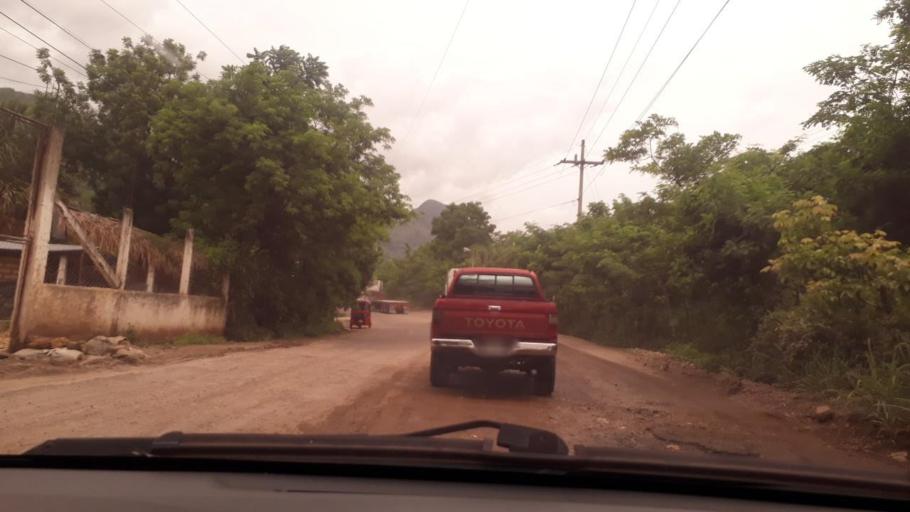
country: GT
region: Chiquimula
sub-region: Municipio de Jocotan
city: Jocotan
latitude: 14.7960
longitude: -89.3962
